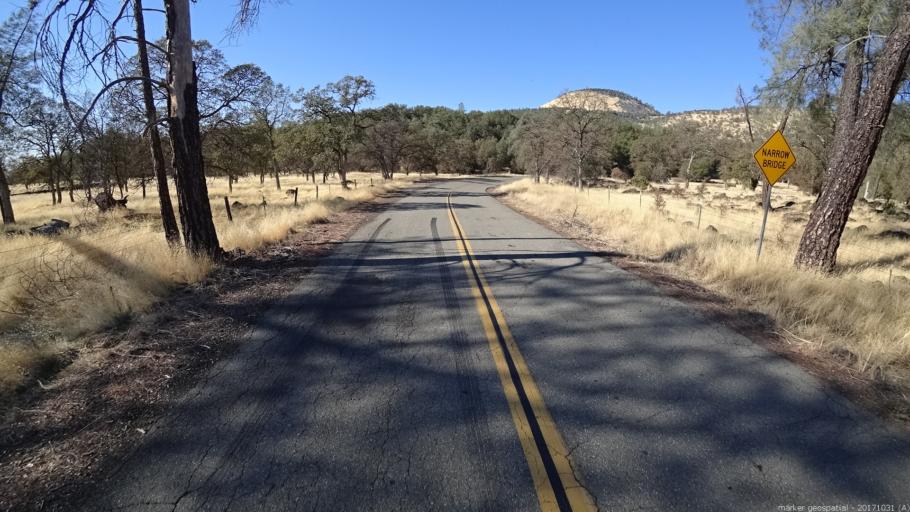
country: US
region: California
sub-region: Shasta County
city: Shingletown
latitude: 40.4382
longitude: -121.9849
